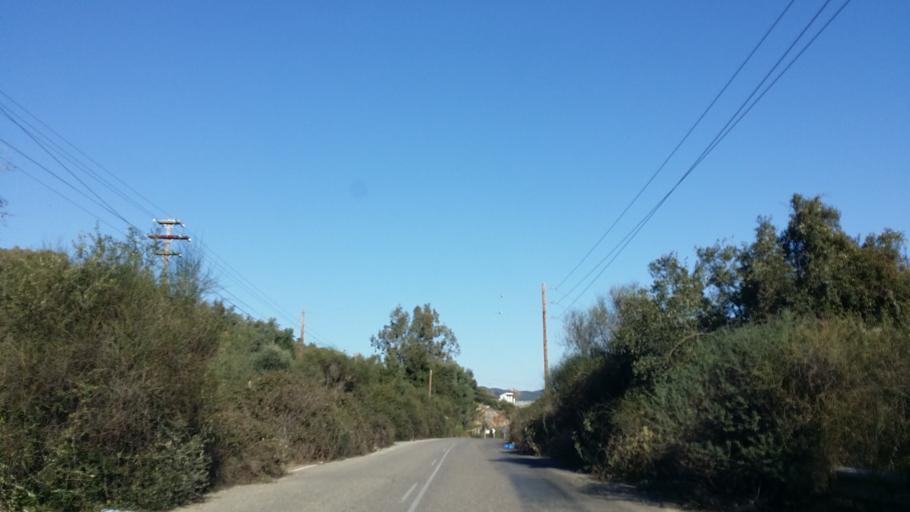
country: GR
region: West Greece
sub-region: Nomos Aitolias kai Akarnanias
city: Neapolis
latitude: 38.6730
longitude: 21.3245
